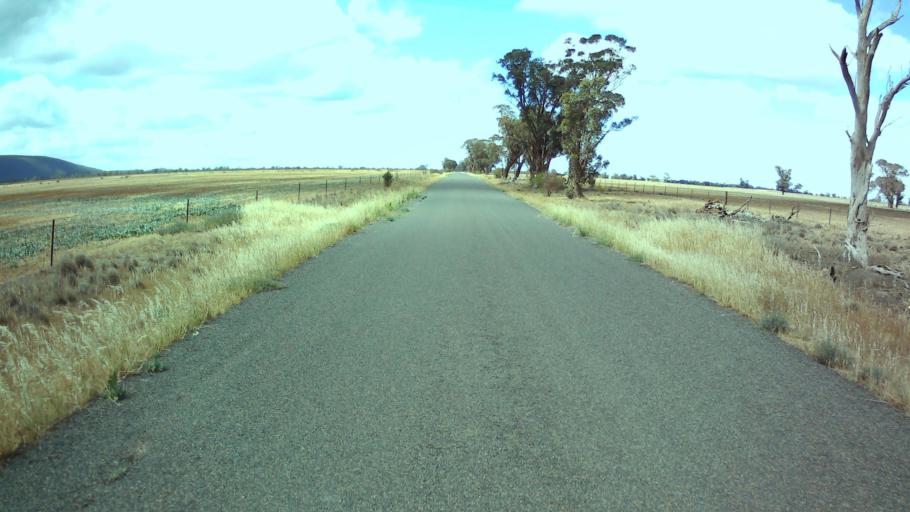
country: AU
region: New South Wales
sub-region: Weddin
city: Grenfell
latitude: -33.8716
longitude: 147.9264
